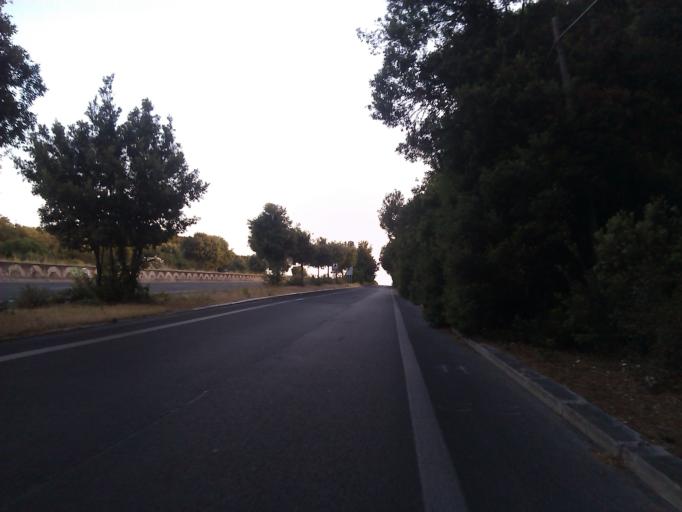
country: IT
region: Latium
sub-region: Citta metropolitana di Roma Capitale
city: Acilia-Castel Fusano-Ostia Antica
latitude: 41.7178
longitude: 12.3212
